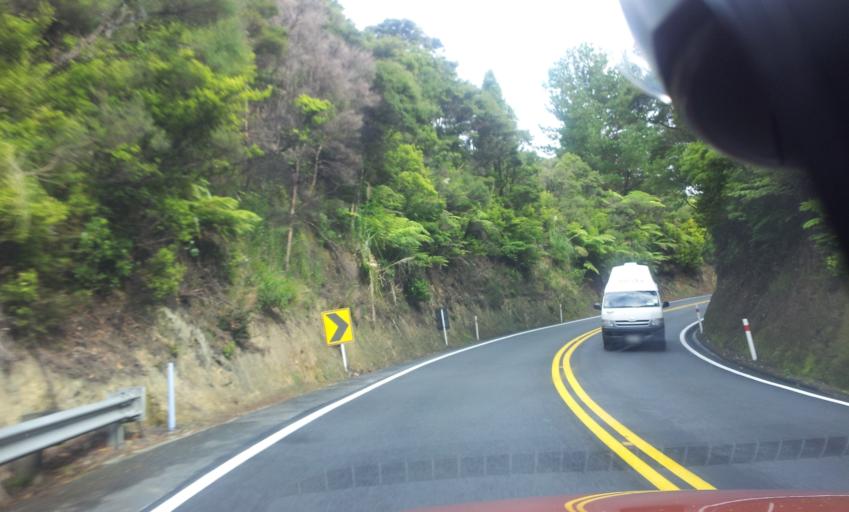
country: NZ
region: Northland
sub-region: Whangarei
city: Ruakaka
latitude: -36.0729
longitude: 174.4194
